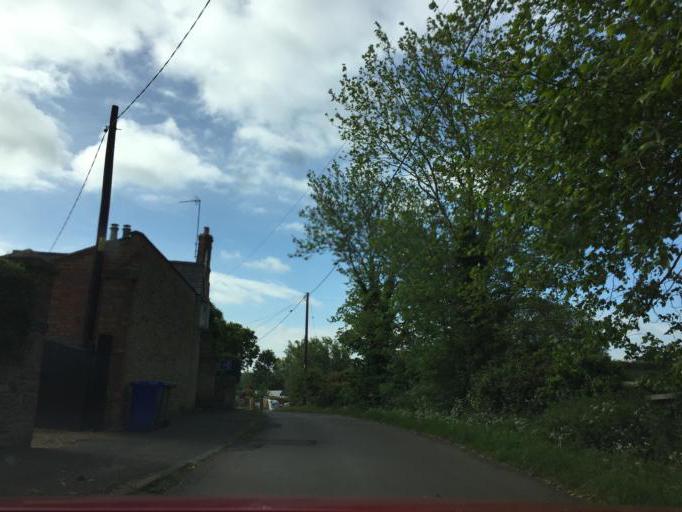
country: GB
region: England
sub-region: Northamptonshire
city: Blisworth
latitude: 52.1427
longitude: -0.9408
